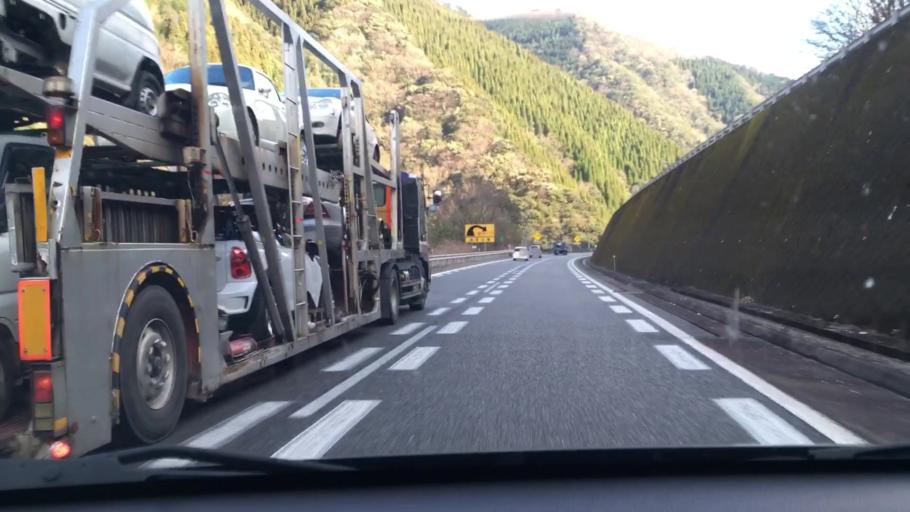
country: JP
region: Kumamoto
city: Hitoyoshi
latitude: 32.3274
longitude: 130.7534
